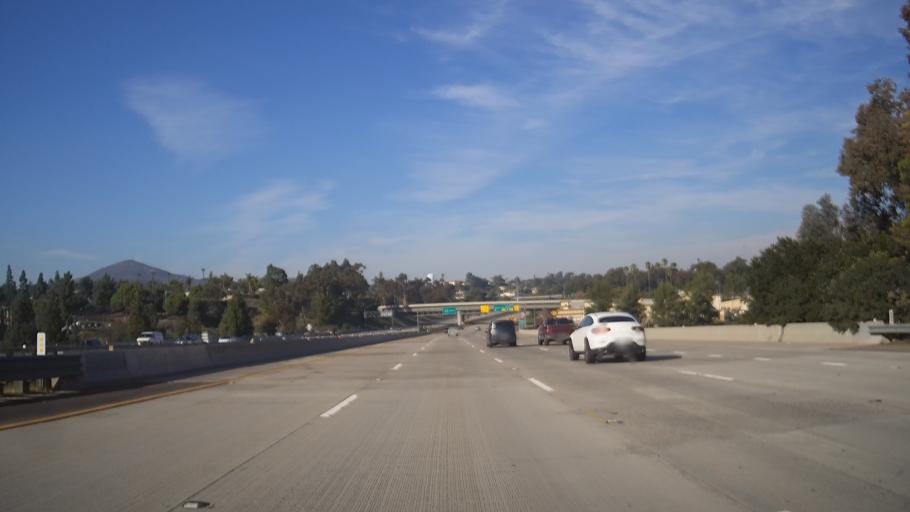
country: US
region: California
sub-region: San Diego County
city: La Mesa
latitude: 32.7833
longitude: -117.0053
